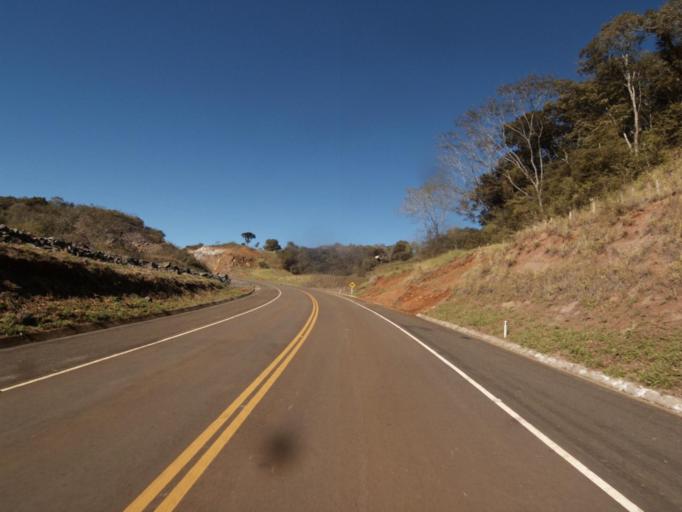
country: AR
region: Misiones
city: Bernardo de Irigoyen
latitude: -26.6133
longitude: -53.7231
